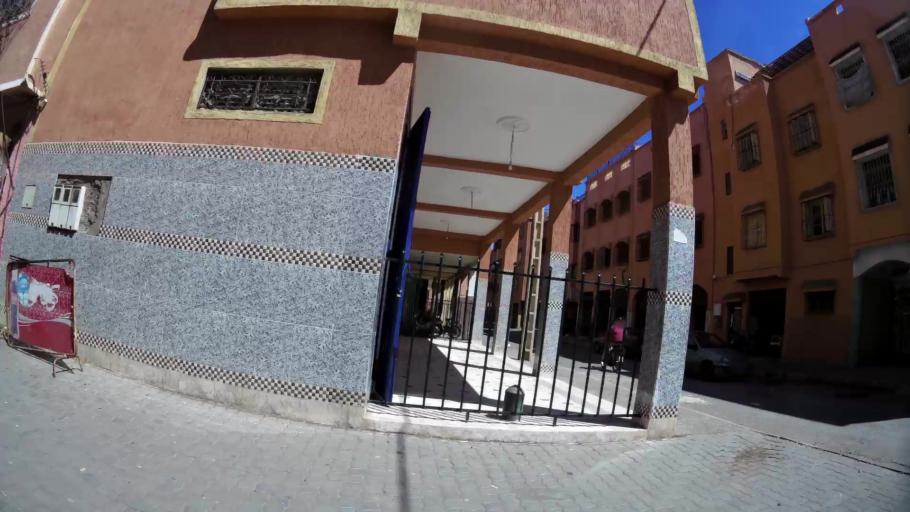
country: MA
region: Marrakech-Tensift-Al Haouz
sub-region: Marrakech
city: Marrakesh
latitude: 31.6309
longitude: -8.0682
